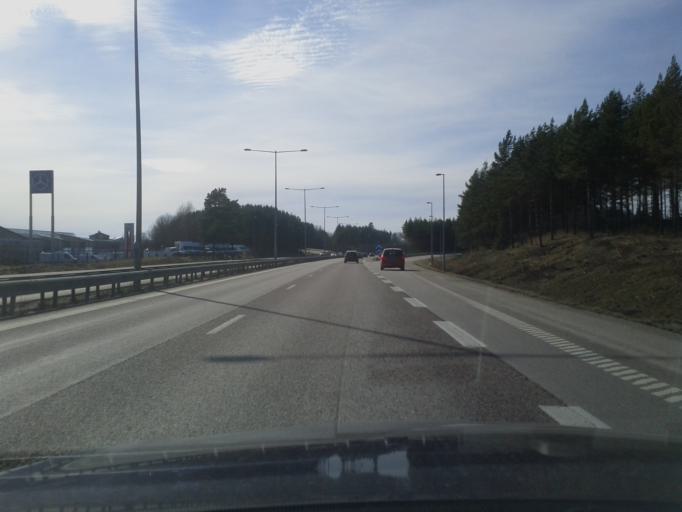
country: SE
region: Vaestmanland
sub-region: Vasteras
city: Tillberga
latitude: 59.6115
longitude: 16.6364
